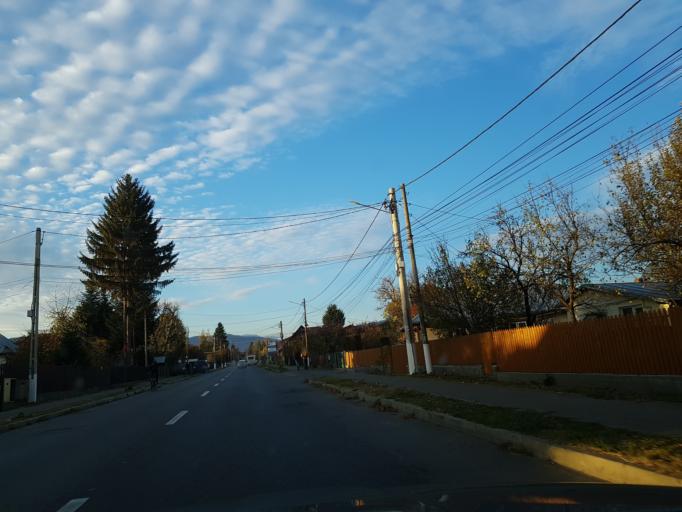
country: RO
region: Prahova
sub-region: Oras Breaza
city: Breaza
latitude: 45.1876
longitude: 25.6616
